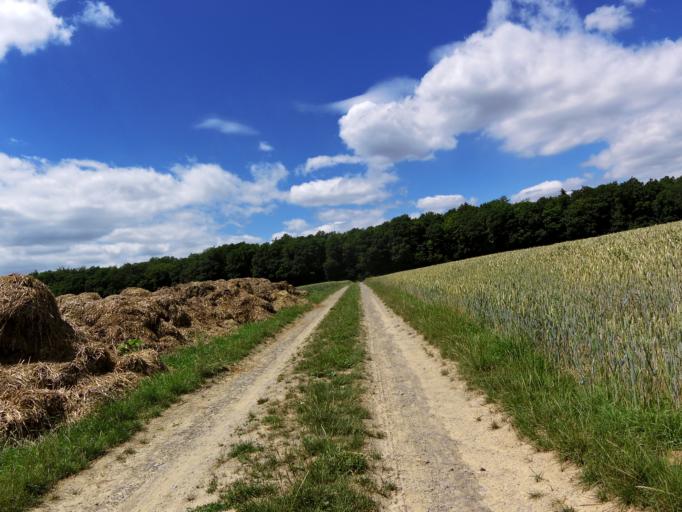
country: DE
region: Bavaria
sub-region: Regierungsbezirk Unterfranken
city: Kist
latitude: 49.7325
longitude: 9.8373
